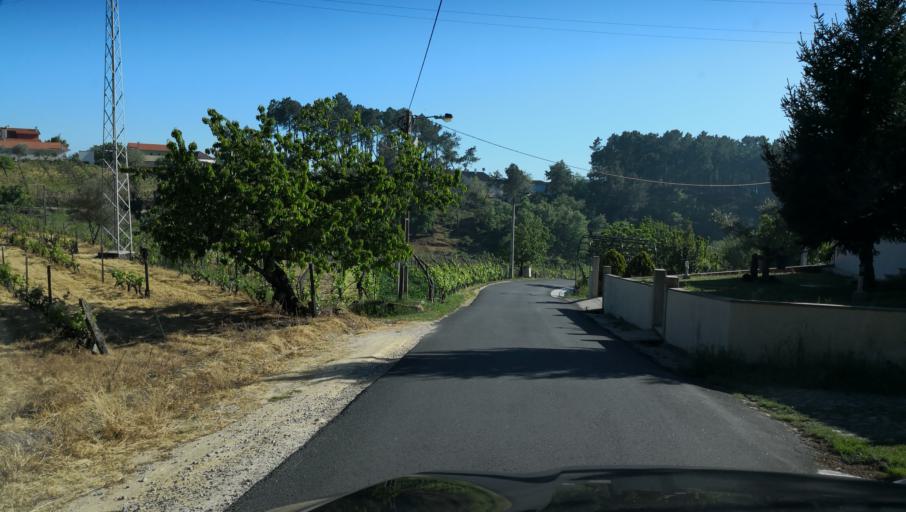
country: PT
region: Vila Real
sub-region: Vila Real
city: Vila Real
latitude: 41.3355
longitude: -7.7310
